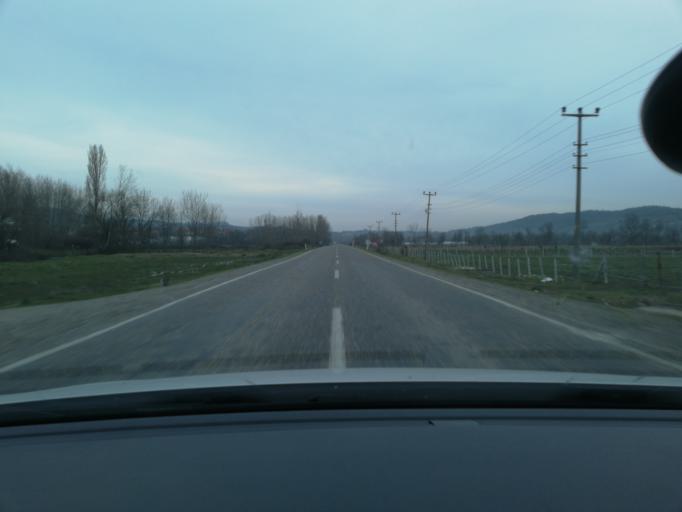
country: TR
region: Zonguldak
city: Saltukova
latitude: 41.5076
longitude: 32.1004
